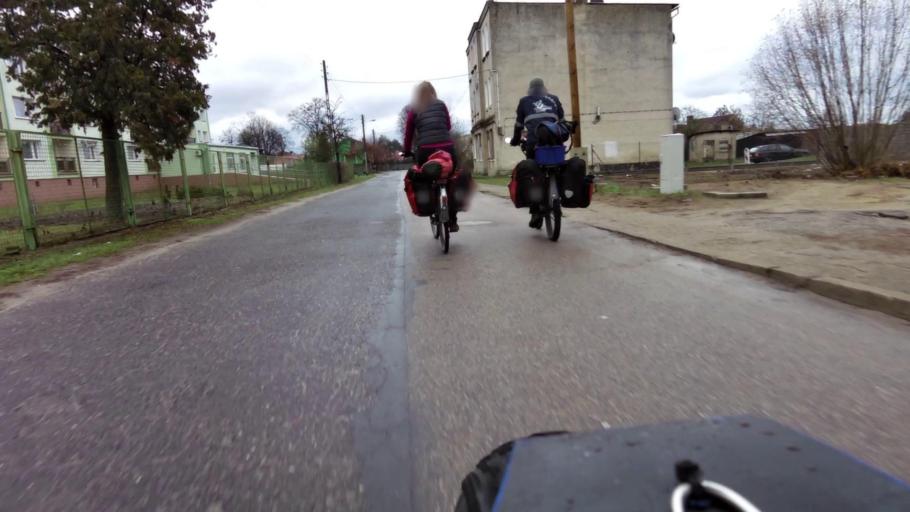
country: PL
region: Lubusz
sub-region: Powiat gorzowski
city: Witnica
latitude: 52.6846
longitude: 14.8862
